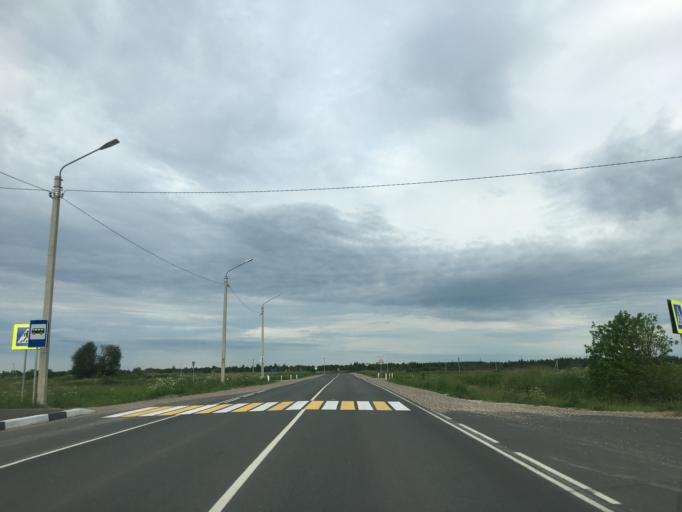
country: RU
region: Pskov
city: Izborsk
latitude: 57.8358
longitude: 28.0538
